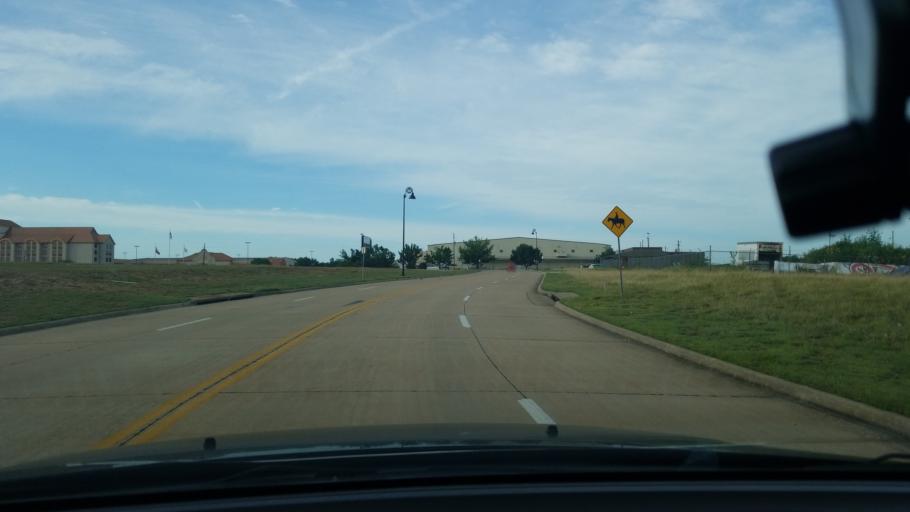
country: US
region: Texas
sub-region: Dallas County
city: Mesquite
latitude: 32.7649
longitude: -96.6258
